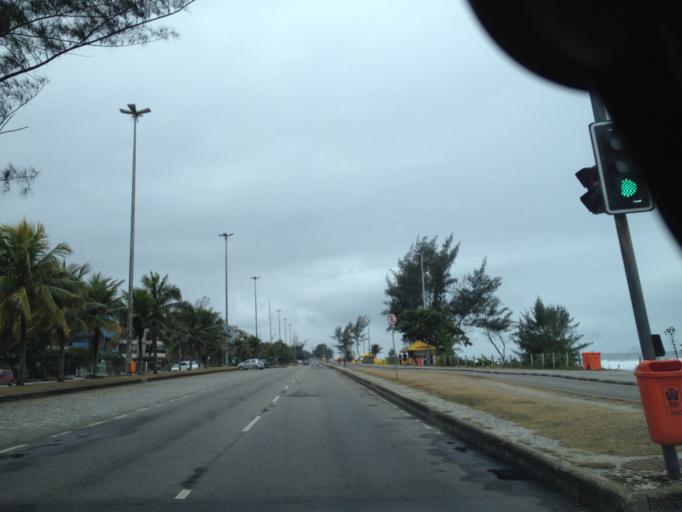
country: BR
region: Rio de Janeiro
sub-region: Nilopolis
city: Nilopolis
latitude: -23.0240
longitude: -43.4534
